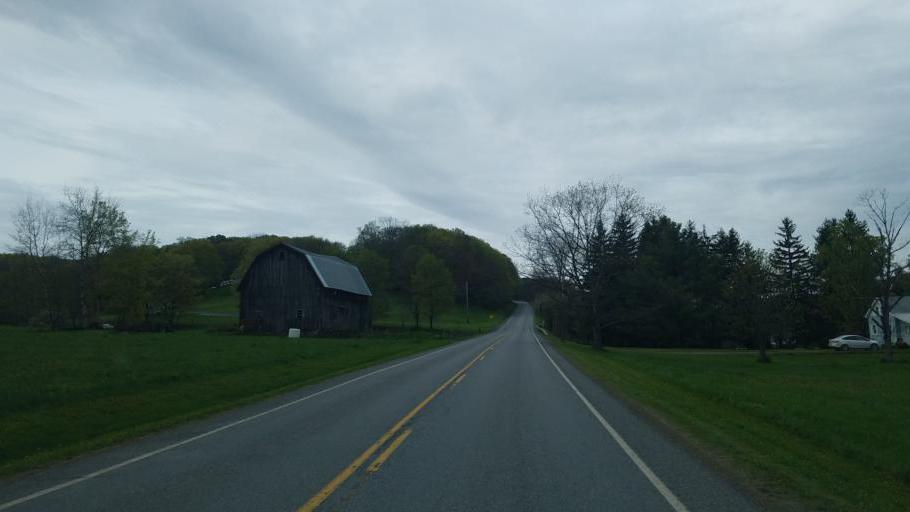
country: US
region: Pennsylvania
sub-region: Tioga County
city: Westfield
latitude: 41.9419
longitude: -77.7048
